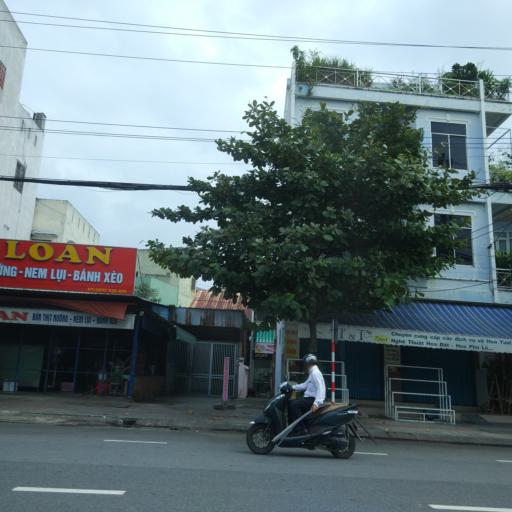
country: VN
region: Da Nang
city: Son Tra
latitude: 16.0672
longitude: 108.2328
